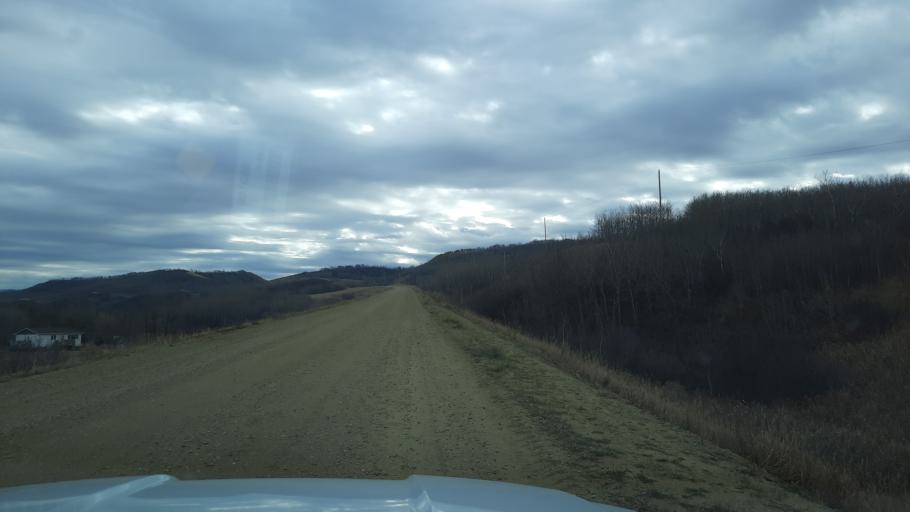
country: CA
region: Saskatchewan
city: Pilot Butte
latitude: 50.7755
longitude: -104.2826
